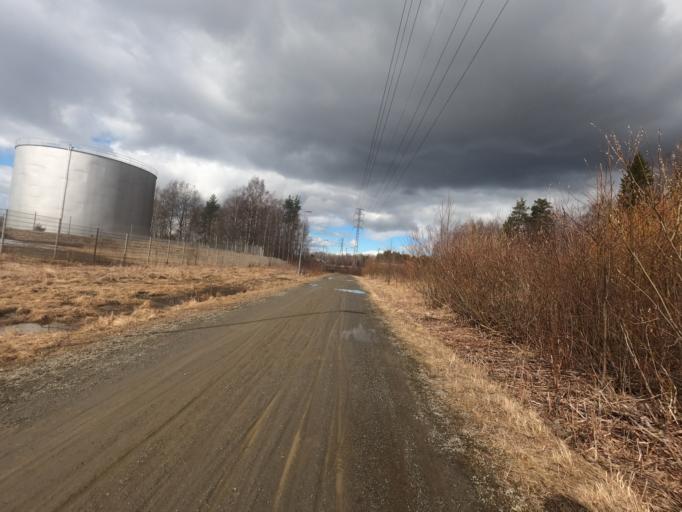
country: FI
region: North Karelia
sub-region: Joensuu
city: Joensuu
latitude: 62.6051
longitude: 29.7846
